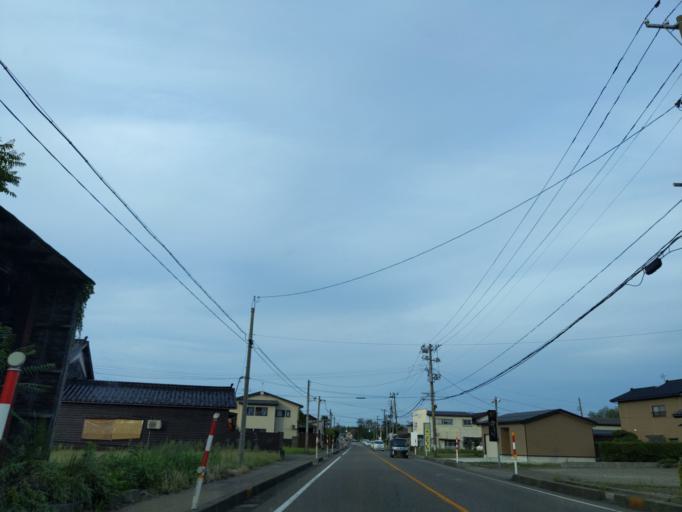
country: JP
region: Niigata
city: Joetsu
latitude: 37.2249
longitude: 138.3271
